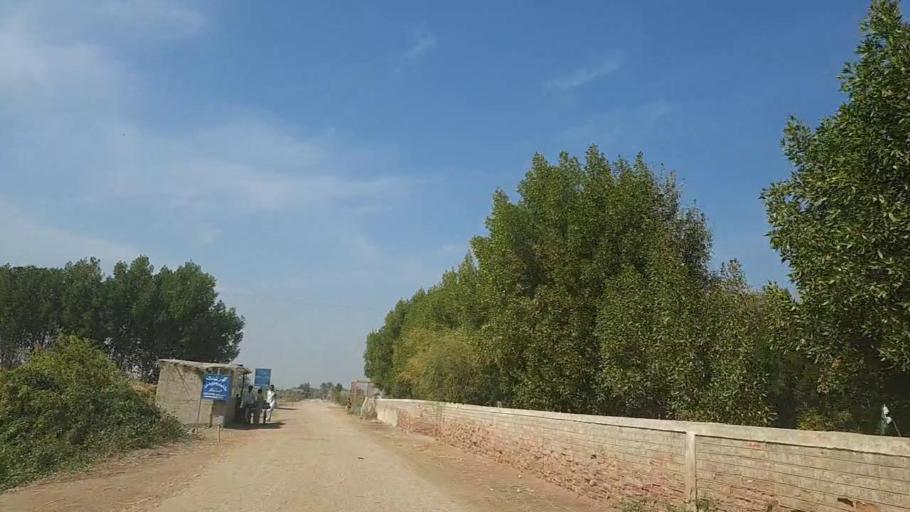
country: PK
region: Sindh
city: Mirpur Khas
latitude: 25.4811
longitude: 68.9706
